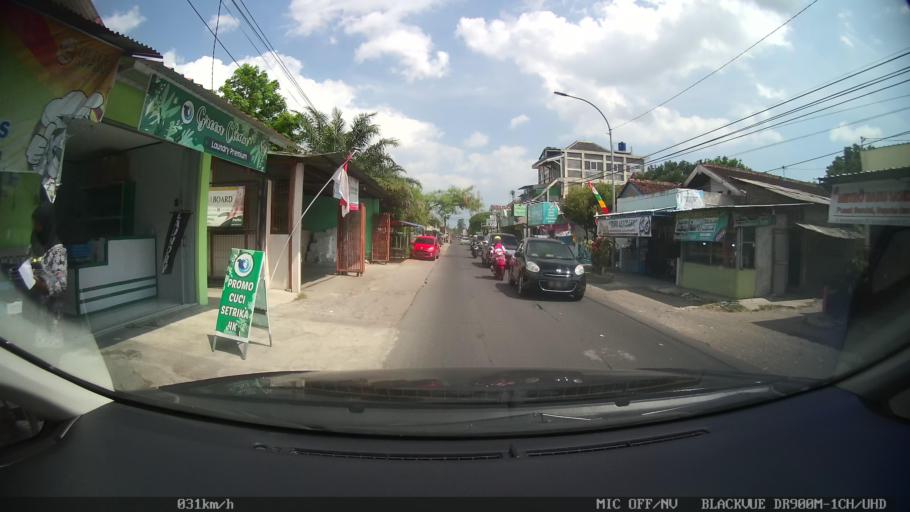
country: ID
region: Daerah Istimewa Yogyakarta
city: Gamping Lor
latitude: -7.8093
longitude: 110.3386
